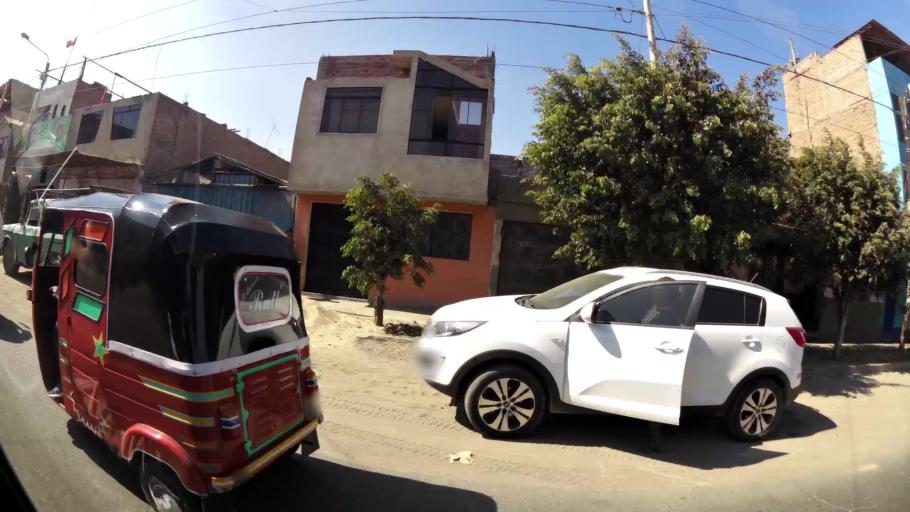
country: PE
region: Ica
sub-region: Provincia de Ica
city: La Tinguina
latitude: -14.0516
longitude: -75.7041
